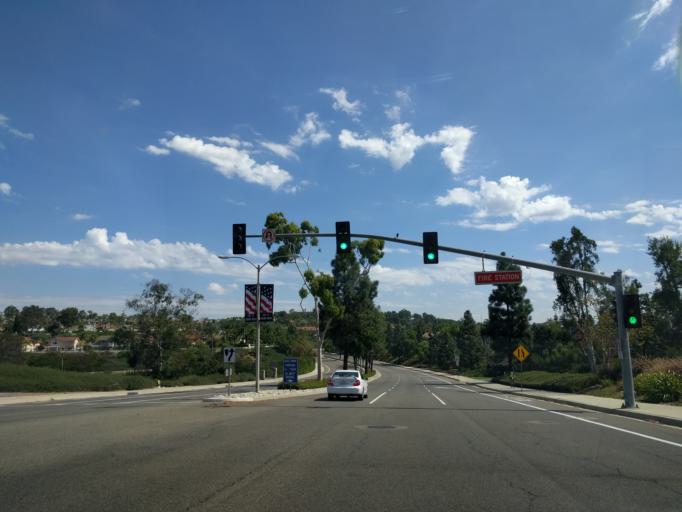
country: US
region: California
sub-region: Orange County
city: San Juan Capistrano
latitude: 33.5056
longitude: -117.6874
